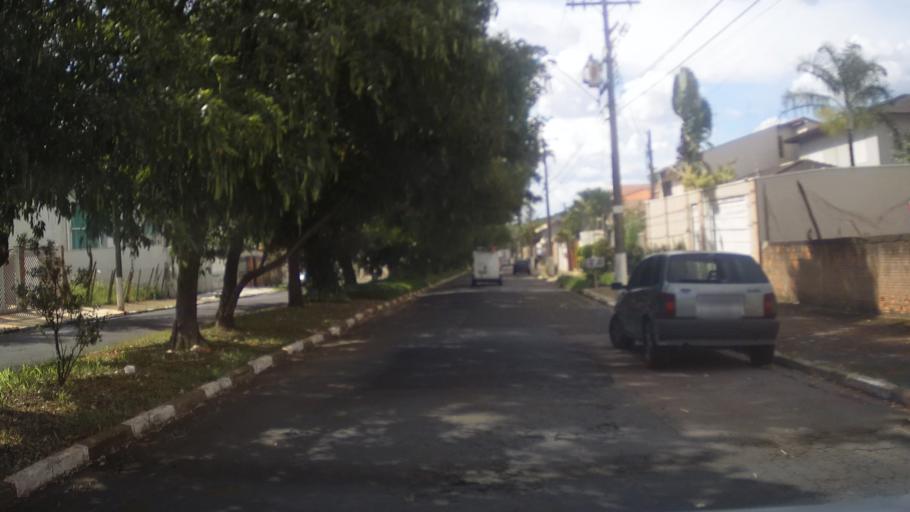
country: BR
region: Sao Paulo
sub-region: Campinas
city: Campinas
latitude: -22.8910
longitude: -47.0927
